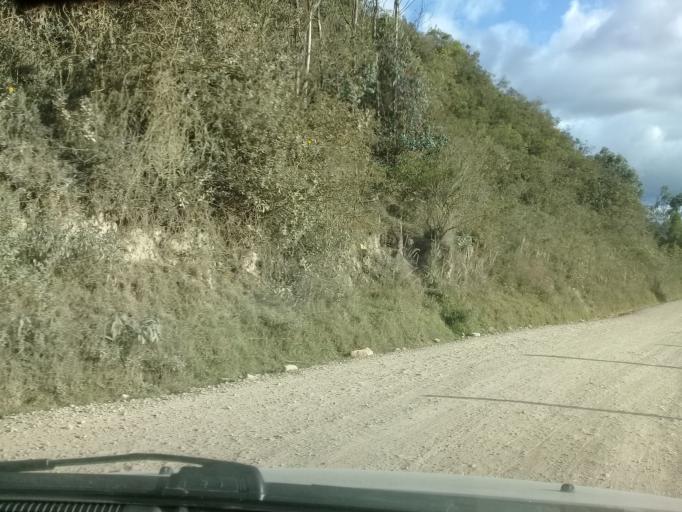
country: CO
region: Cundinamarca
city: Villapinzon
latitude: 5.2236
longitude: -73.6447
